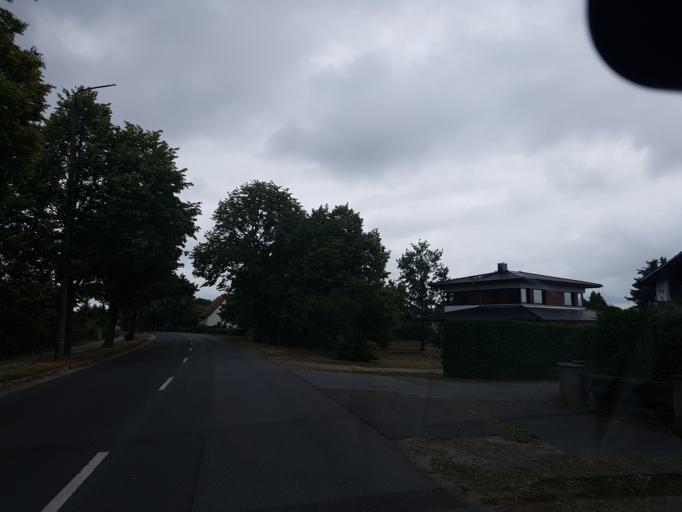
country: DE
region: Brandenburg
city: Luckau
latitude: 51.8451
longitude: 13.6994
